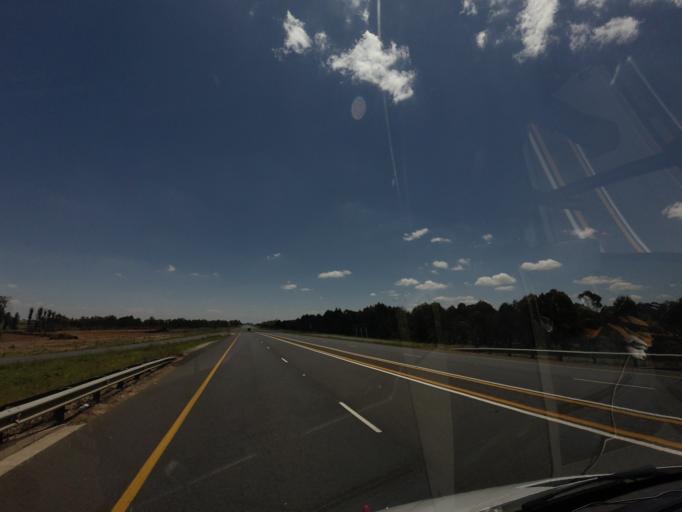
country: ZA
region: Mpumalanga
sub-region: Nkangala District Municipality
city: Belfast
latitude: -25.7168
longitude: 30.0537
